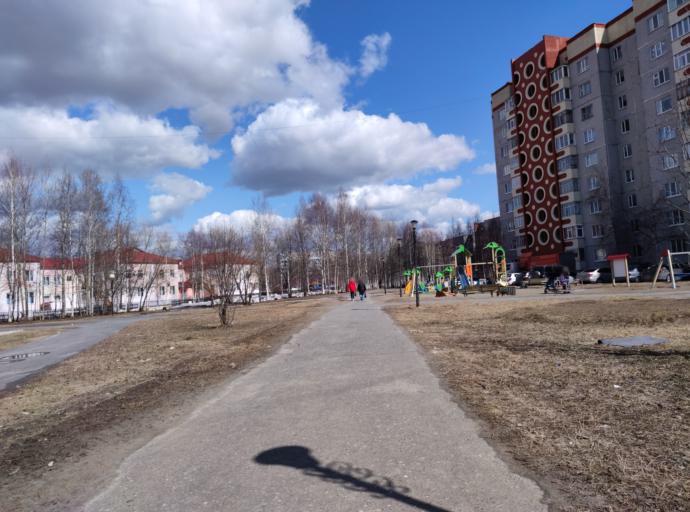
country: RU
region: Khanty-Mansiyskiy Avtonomnyy Okrug
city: Langepas
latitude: 61.2511
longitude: 75.1805
